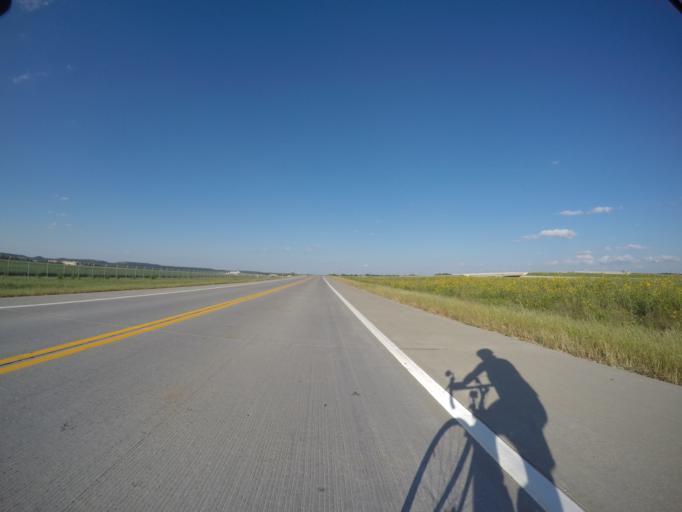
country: US
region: Kansas
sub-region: Riley County
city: Ogden
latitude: 39.1295
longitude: -96.6769
